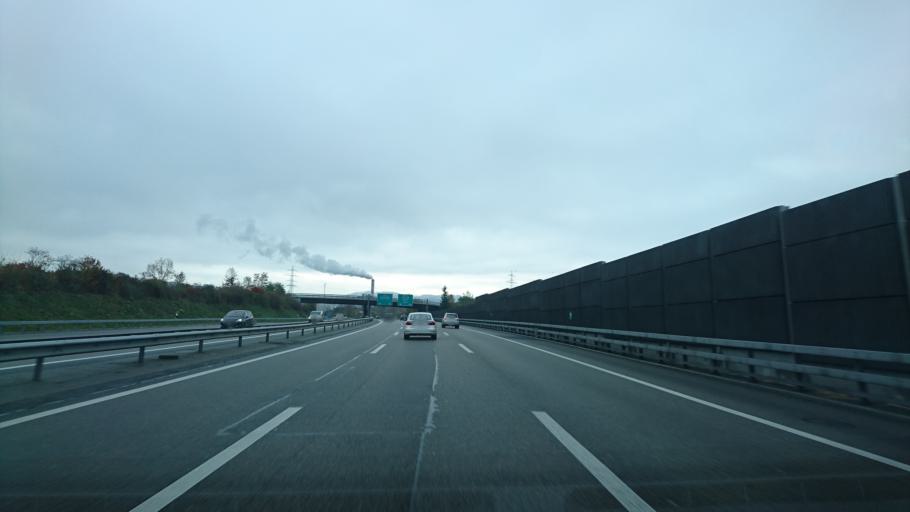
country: CH
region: Aargau
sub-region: Bezirk Zofingen
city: Oftringen
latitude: 47.3054
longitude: 7.9123
